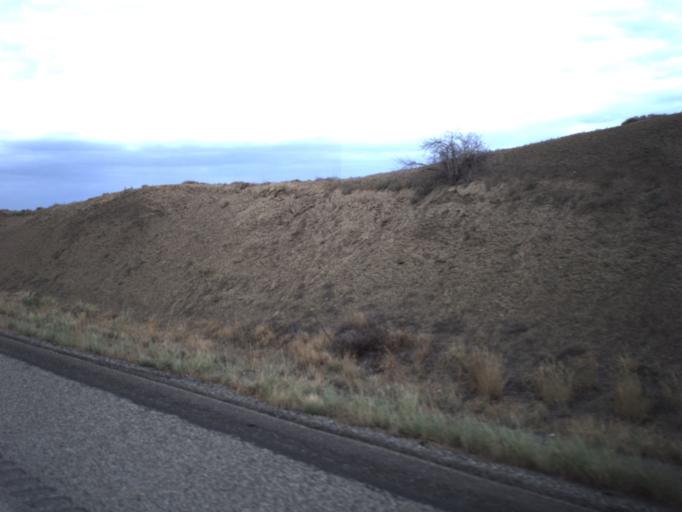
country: US
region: Colorado
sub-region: Mesa County
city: Loma
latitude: 39.1284
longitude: -109.1639
